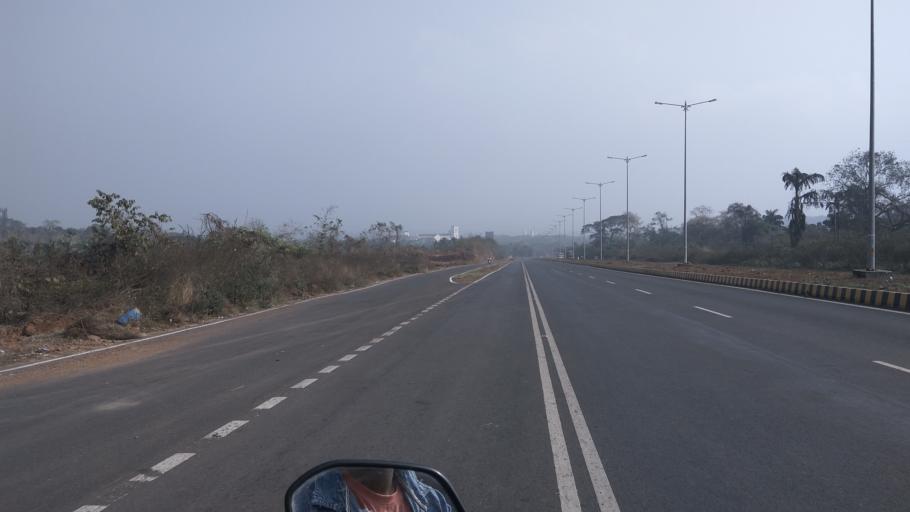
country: IN
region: Goa
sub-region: North Goa
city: Goa Velha
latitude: 15.4924
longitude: 73.9078
